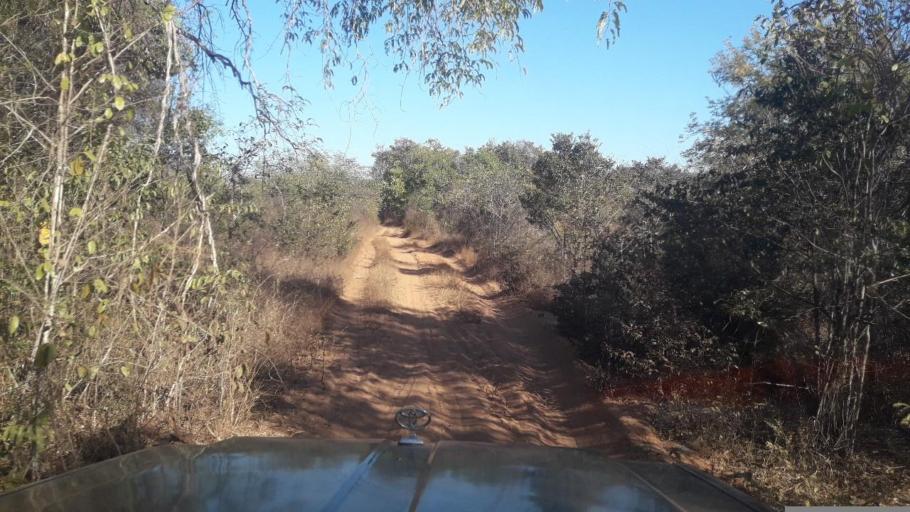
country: MG
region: Boeny
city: Sitampiky
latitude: -16.4222
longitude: 45.6189
